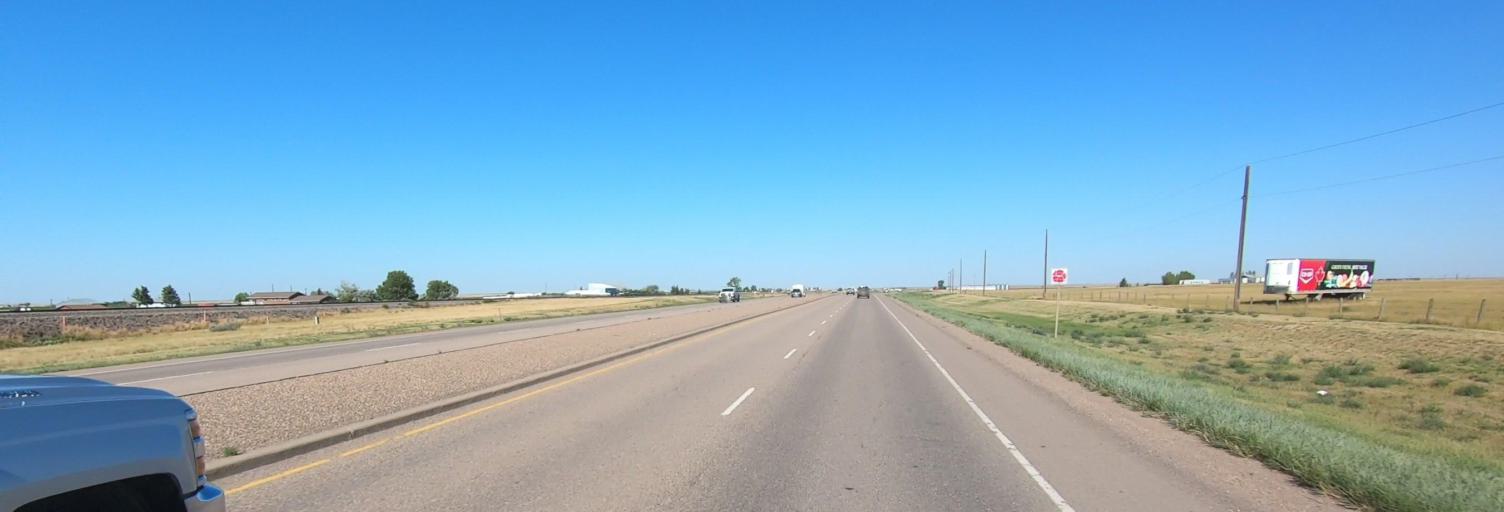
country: CA
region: Alberta
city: Medicine Hat
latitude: 50.0868
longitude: -110.7914
